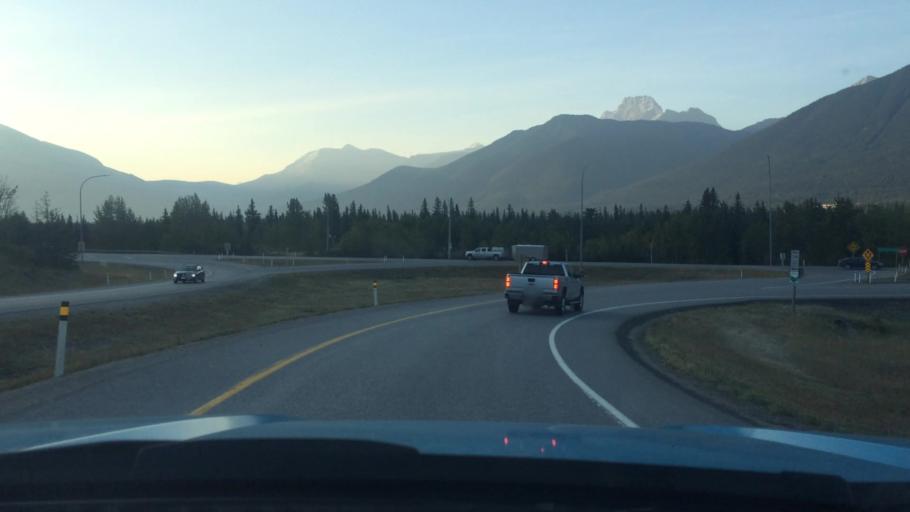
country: CA
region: Alberta
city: Canmore
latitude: 51.0760
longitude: -115.3285
